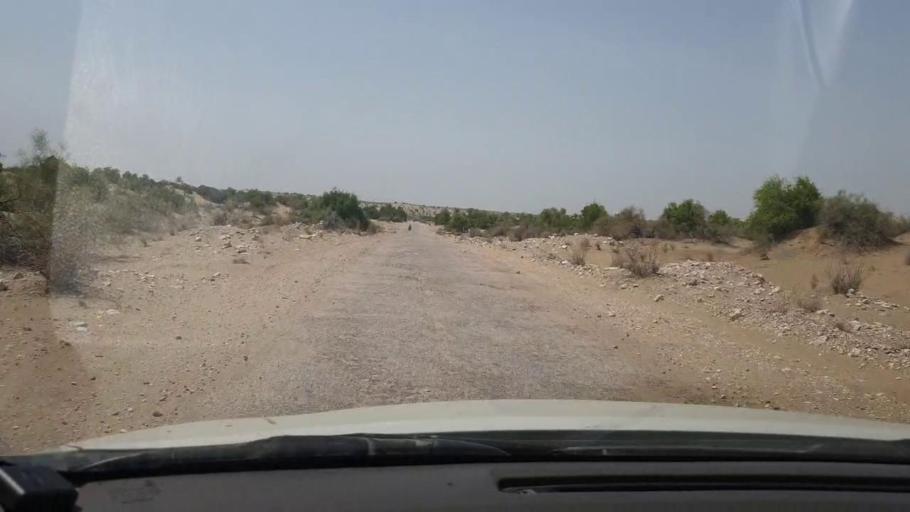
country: PK
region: Sindh
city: Rohri
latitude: 27.3131
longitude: 69.2817
